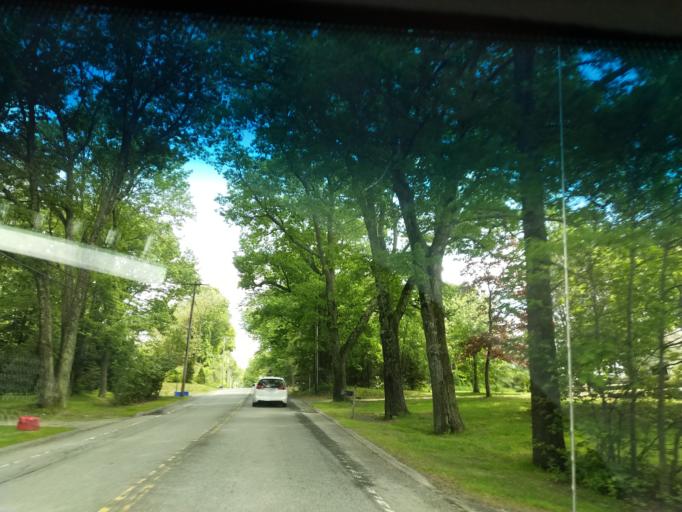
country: US
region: Maine
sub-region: Cumberland County
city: Falmouth
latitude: 43.7362
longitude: -70.2829
